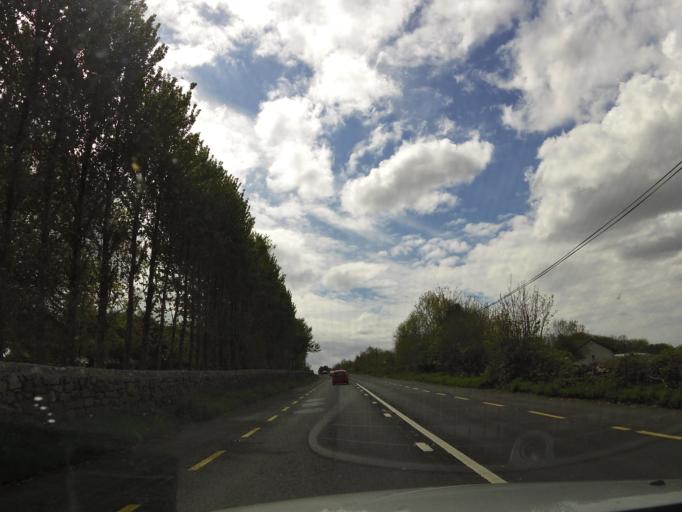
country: IE
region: Connaught
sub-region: County Galway
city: Claregalway
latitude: 53.3217
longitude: -8.9749
